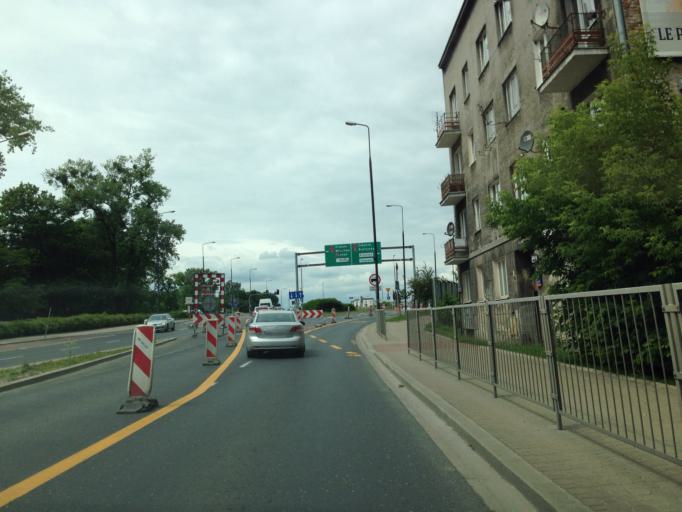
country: PL
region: Masovian Voivodeship
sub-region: Warszawa
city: Zoliborz
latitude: 52.2614
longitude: 20.9557
